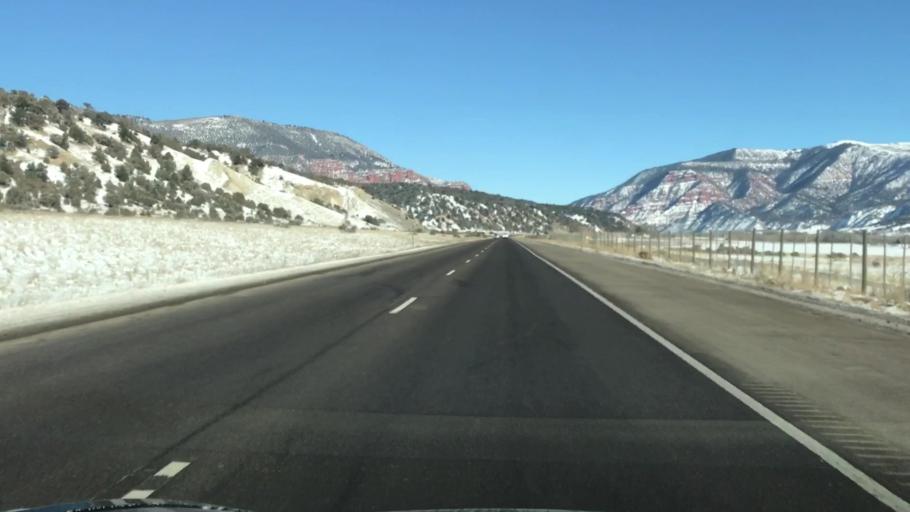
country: US
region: Colorado
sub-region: Eagle County
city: Eagle
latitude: 39.6688
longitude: -106.8082
